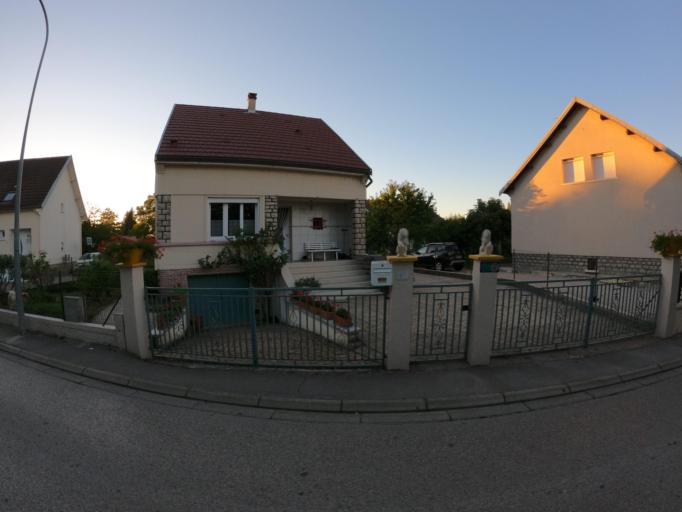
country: FR
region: Franche-Comte
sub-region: Departement du Jura
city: Montmorot
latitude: 46.6749
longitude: 5.5339
